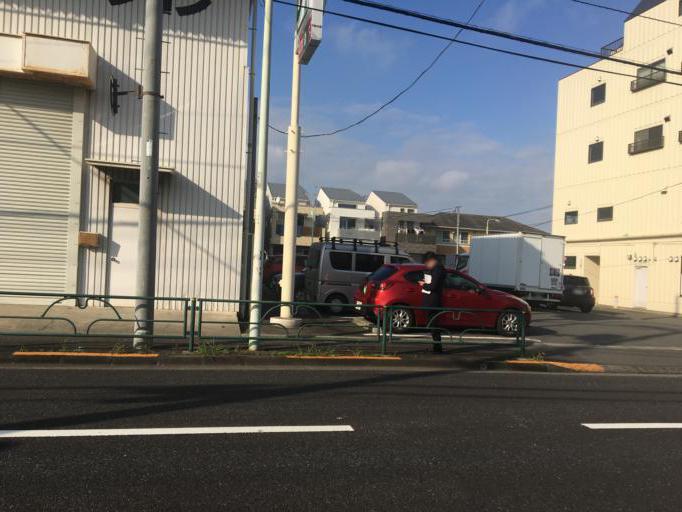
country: JP
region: Tokyo
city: Musashino
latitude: 35.7181
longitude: 139.6015
